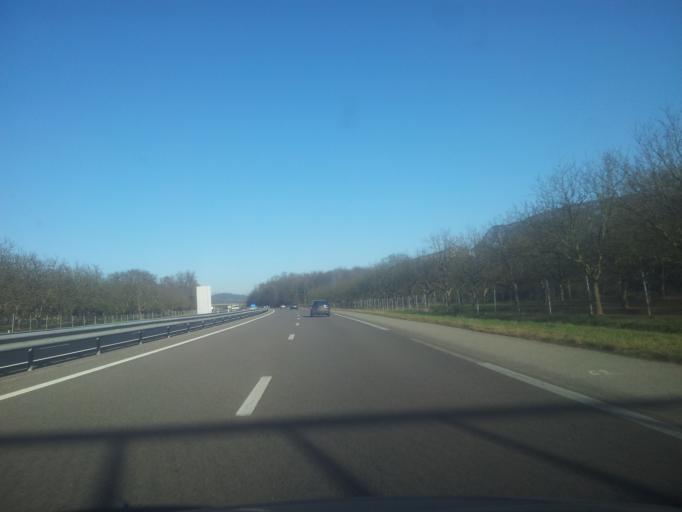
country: FR
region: Rhone-Alpes
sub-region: Departement de l'Isere
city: Vinay
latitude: 45.1871
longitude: 5.4093
